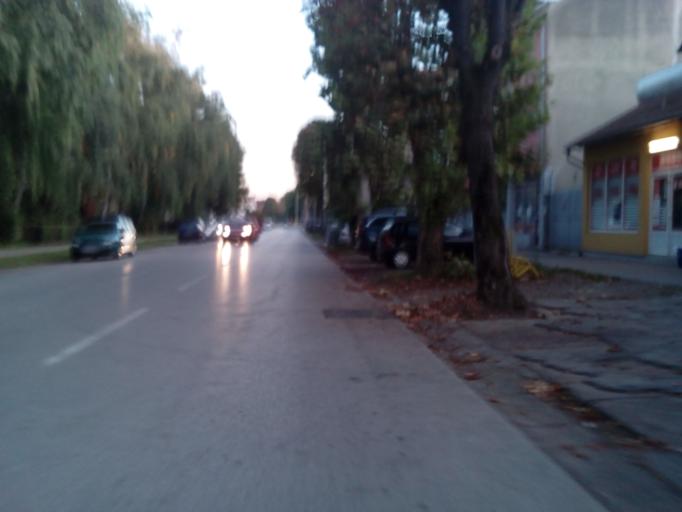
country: HR
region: Vukovarsko-Srijemska
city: Vinkovci
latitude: 45.2984
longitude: 18.8037
